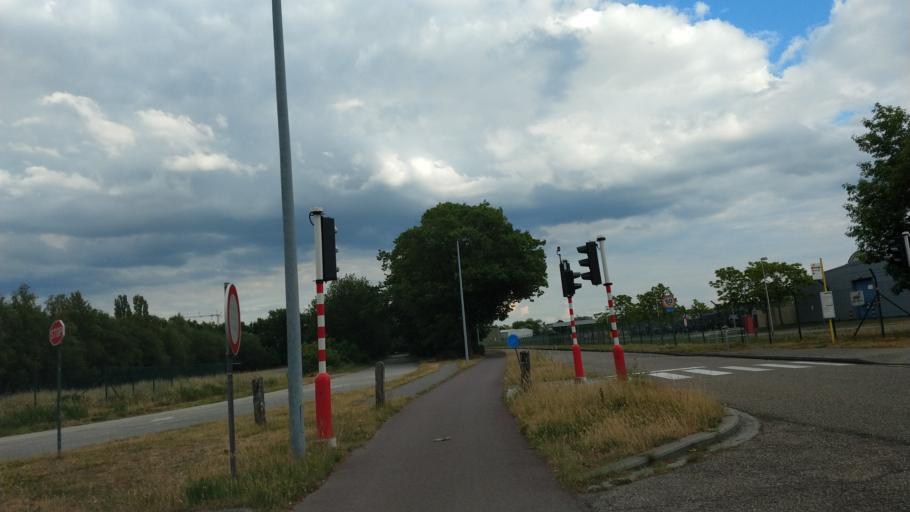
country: BE
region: Flanders
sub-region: Provincie Vlaams-Brabant
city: Leuven
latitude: 50.8527
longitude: 4.7108
